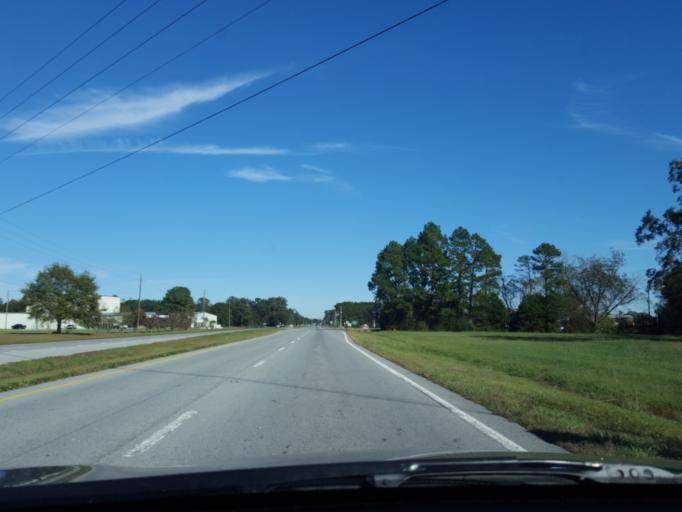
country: US
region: North Carolina
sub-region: Pitt County
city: Greenville
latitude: 35.6233
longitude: -77.2285
